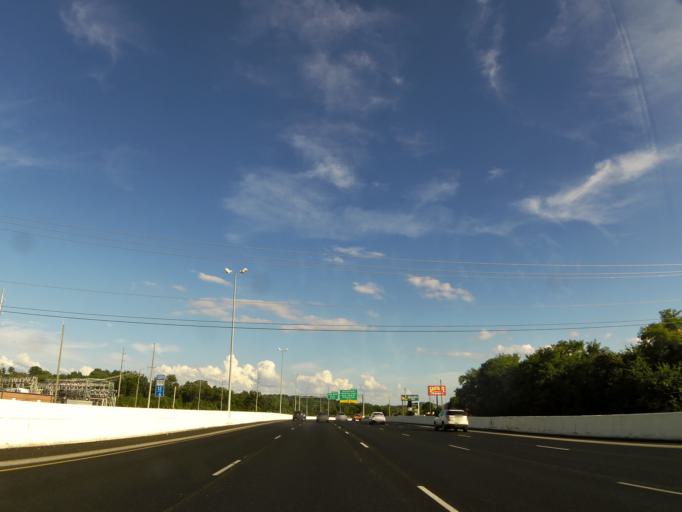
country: US
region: Tennessee
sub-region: Davidson County
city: Lakewood
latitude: 36.2271
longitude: -86.6967
